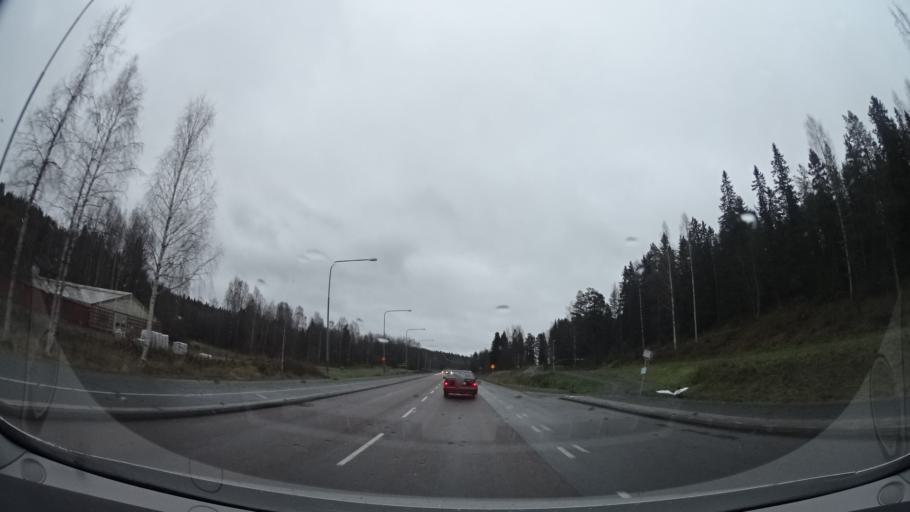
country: SE
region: Vaesterbotten
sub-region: Skelleftea Kommun
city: Skelleftea
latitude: 64.7558
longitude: 20.9846
